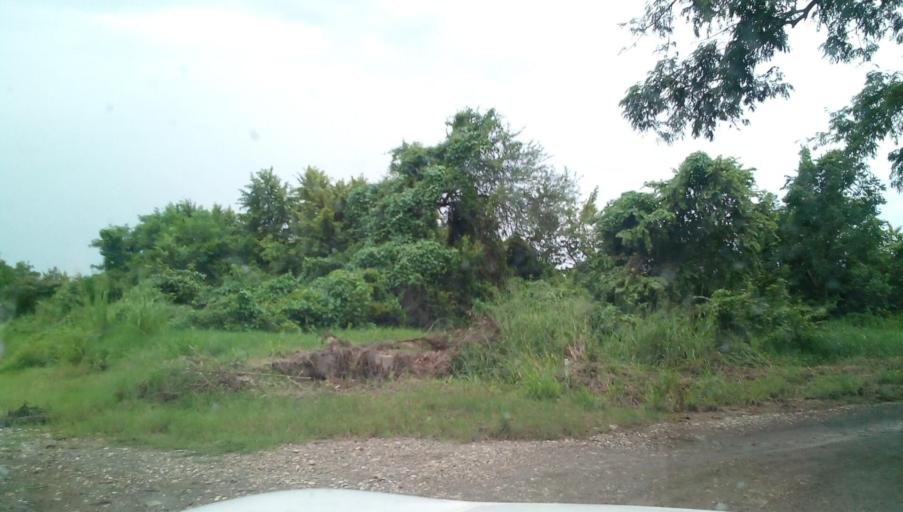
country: MX
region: Veracruz
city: Panuco
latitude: 21.8126
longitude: -98.1123
